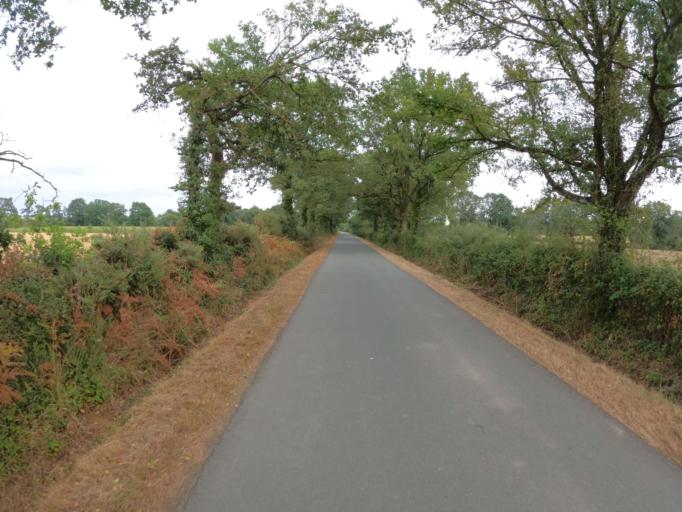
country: FR
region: Pays de la Loire
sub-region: Departement de Maine-et-Loire
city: La Romagne
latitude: 47.0476
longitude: -0.9945
